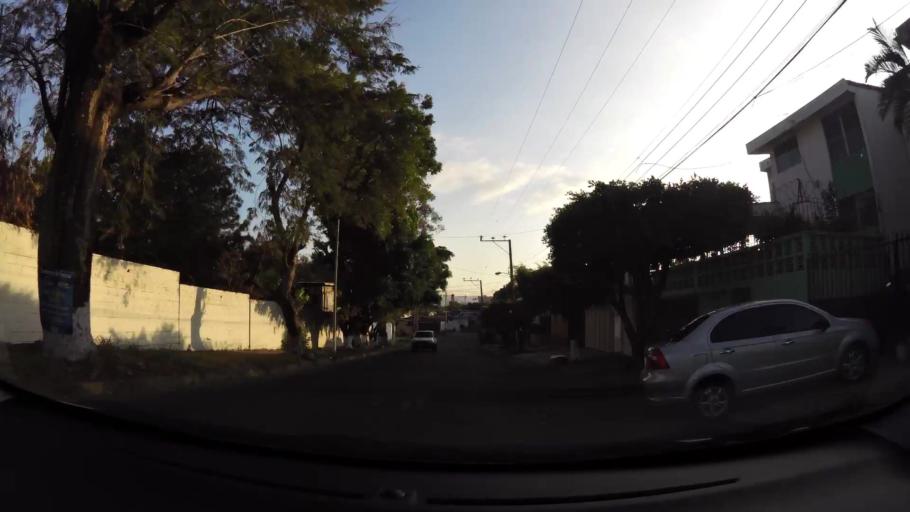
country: SV
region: San Salvador
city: Cuscatancingo
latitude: 13.7169
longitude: -89.1970
